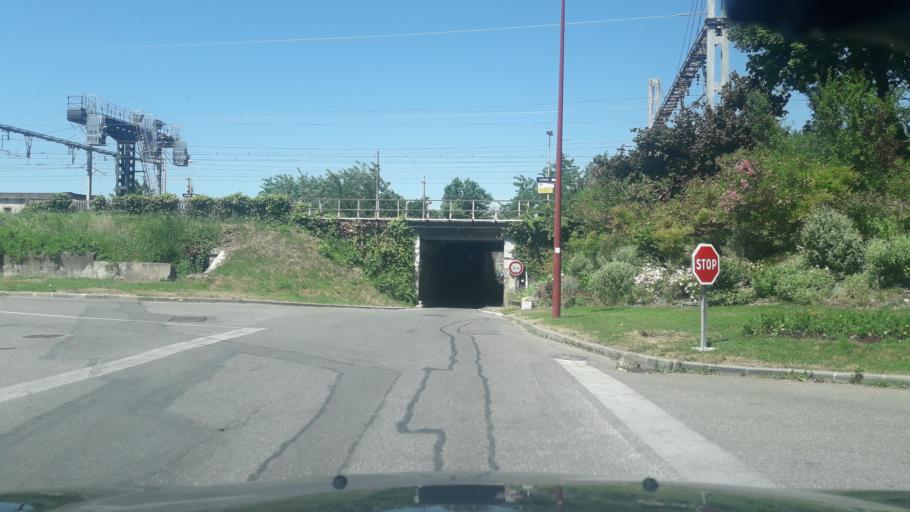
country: FR
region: Rhone-Alpes
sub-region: Departement de la Drome
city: Livron-sur-Drome
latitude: 44.7787
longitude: 4.8303
